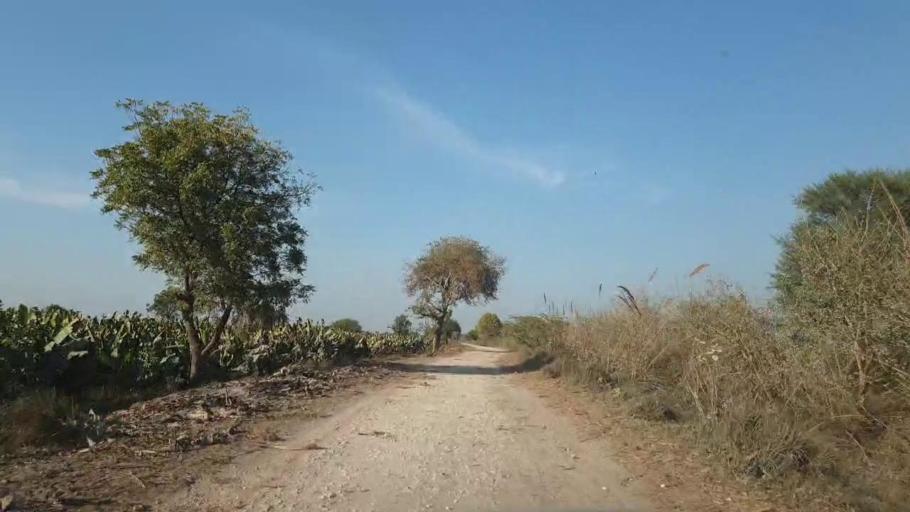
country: PK
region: Sindh
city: Tando Adam
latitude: 25.7158
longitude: 68.7037
